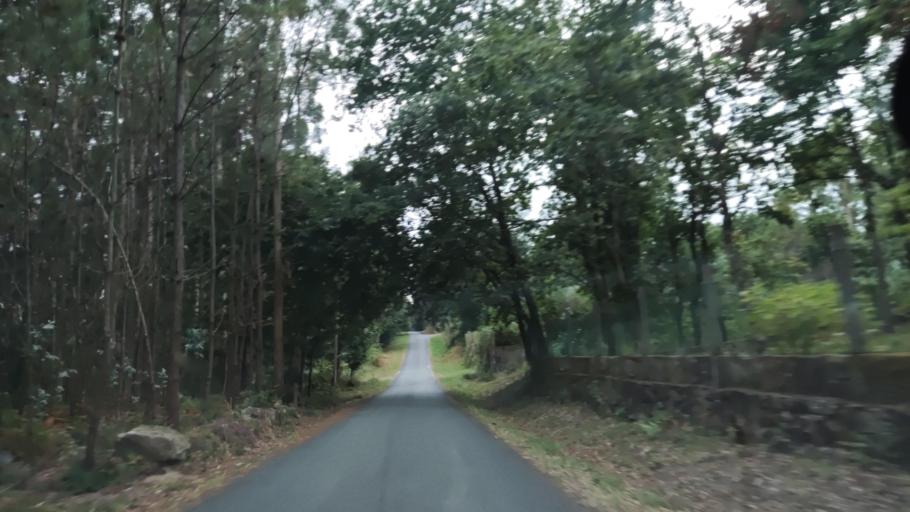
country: ES
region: Galicia
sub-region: Provincia da Coruna
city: Padron
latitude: 42.7199
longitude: -8.6805
